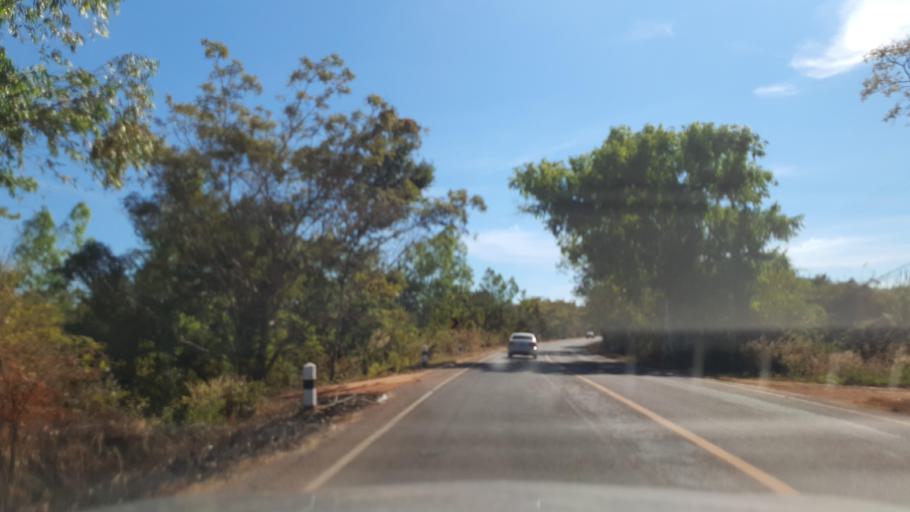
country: TH
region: Kalasin
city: Khao Wong
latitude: 16.8089
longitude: 104.1375
